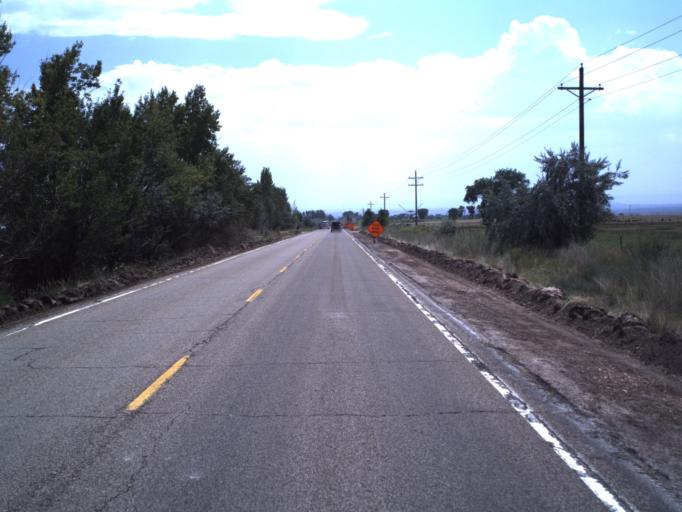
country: US
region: Utah
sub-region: Duchesne County
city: Roosevelt
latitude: 40.4127
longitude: -110.0299
